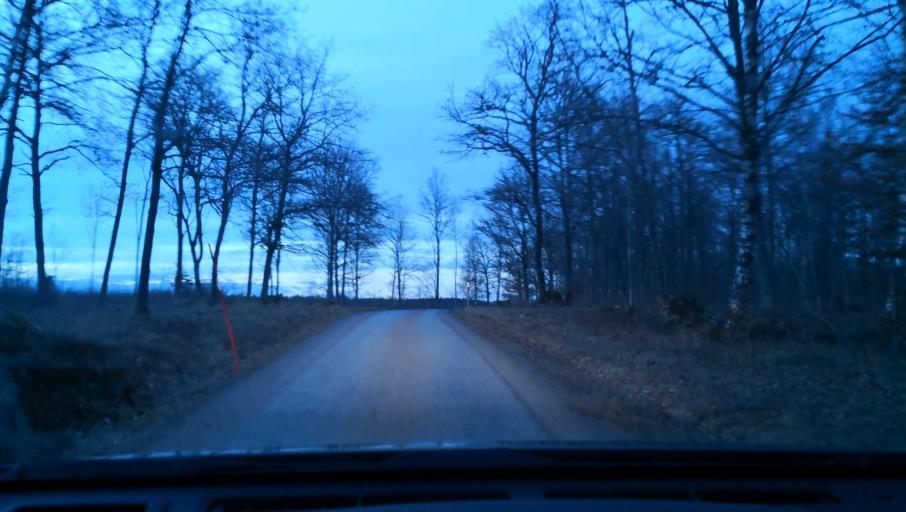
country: SE
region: Uppsala
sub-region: Enkopings Kommun
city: Dalby
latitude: 59.5515
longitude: 17.3685
